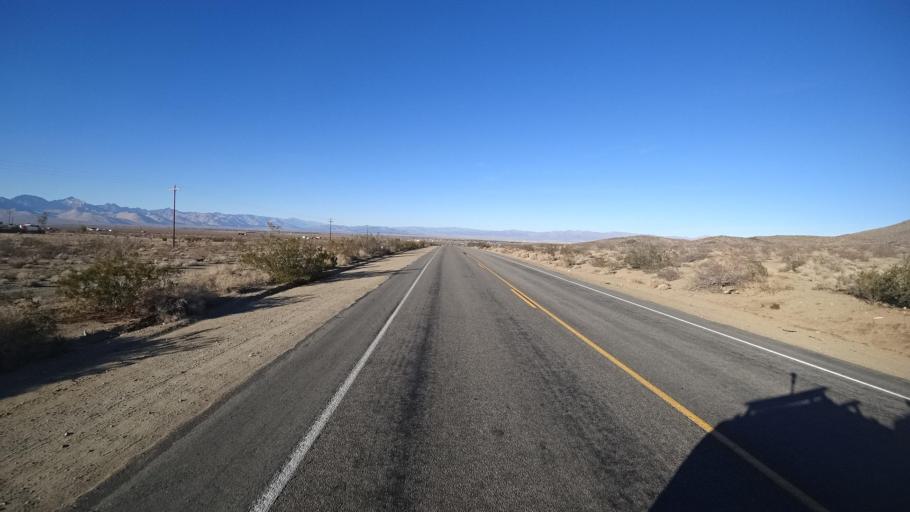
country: US
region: California
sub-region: Kern County
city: Ridgecrest
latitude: 35.5675
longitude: -117.7137
